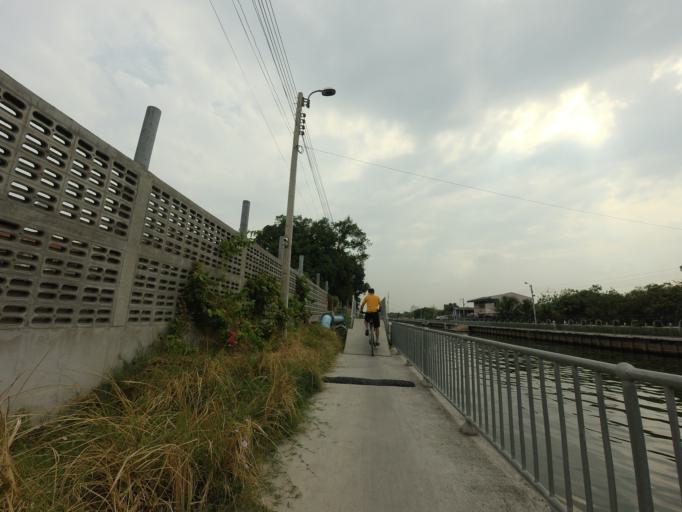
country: TH
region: Bangkok
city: Suan Luang
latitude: 13.7208
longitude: 100.6604
